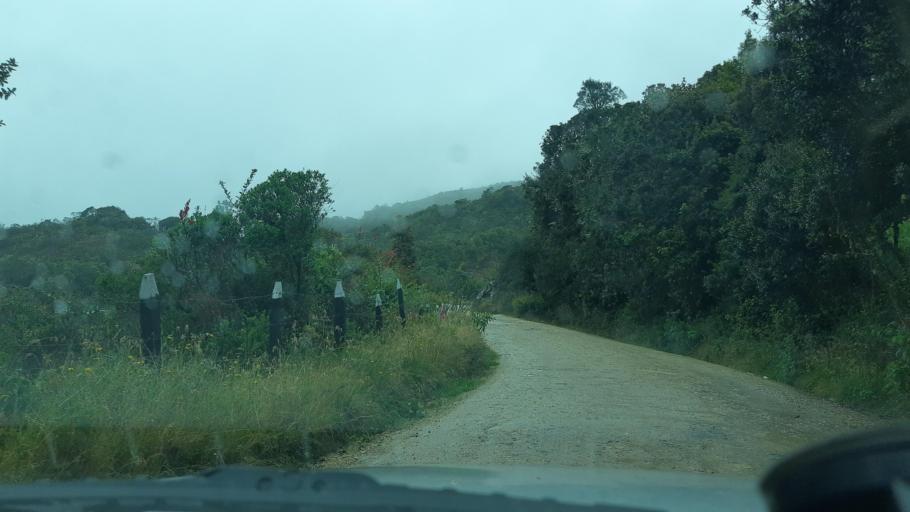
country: CO
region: Cundinamarca
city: Umbita
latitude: 5.2157
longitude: -73.5211
